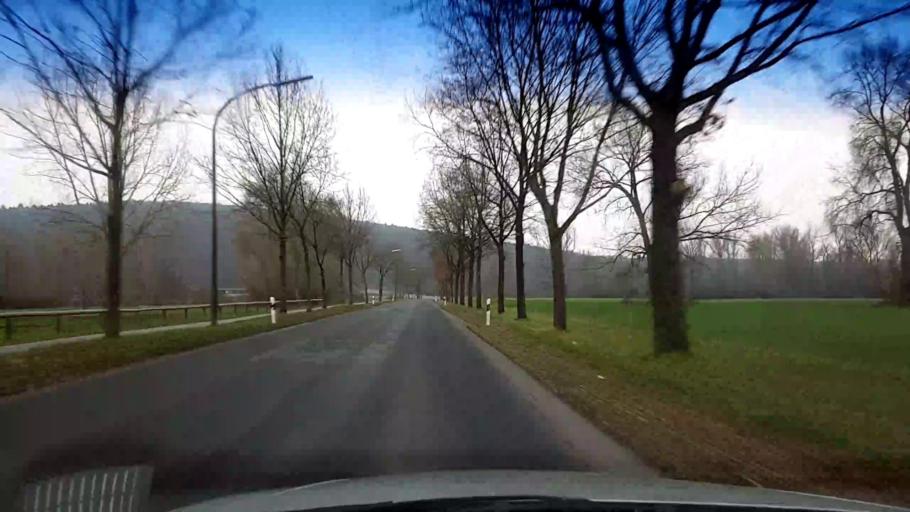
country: DE
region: Bavaria
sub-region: Upper Franconia
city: Rattelsdorf
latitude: 50.0052
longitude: 10.9089
